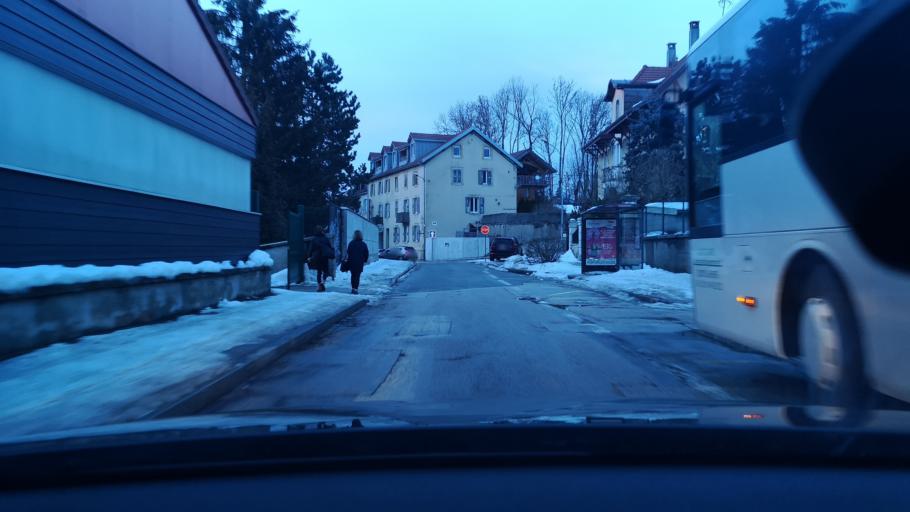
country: FR
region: Franche-Comte
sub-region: Departement du Doubs
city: Pontarlier
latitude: 46.9037
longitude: 6.3602
